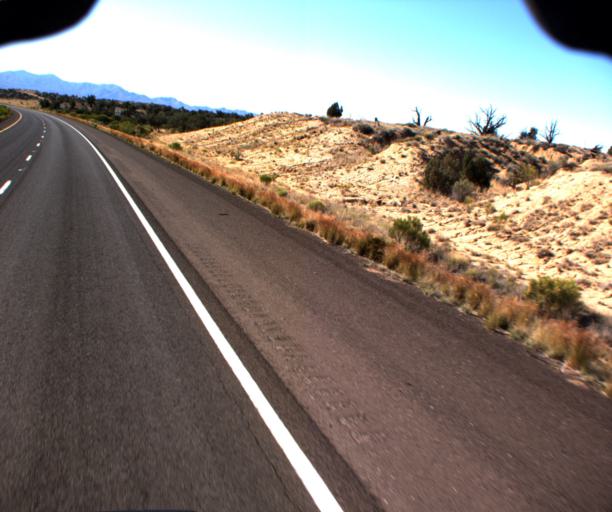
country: US
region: Arizona
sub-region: Mohave County
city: New Kingman-Butler
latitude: 35.1484
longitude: -113.6891
